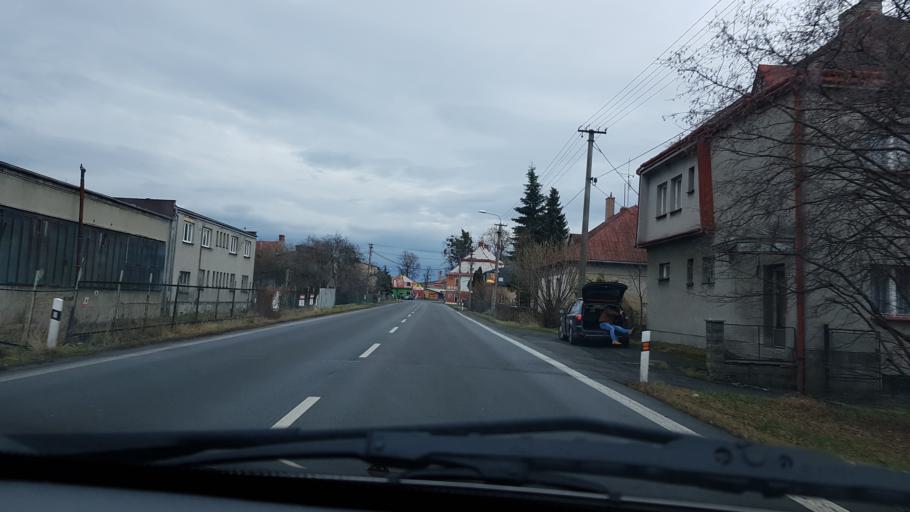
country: CZ
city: Dobra
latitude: 49.6747
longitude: 18.4089
